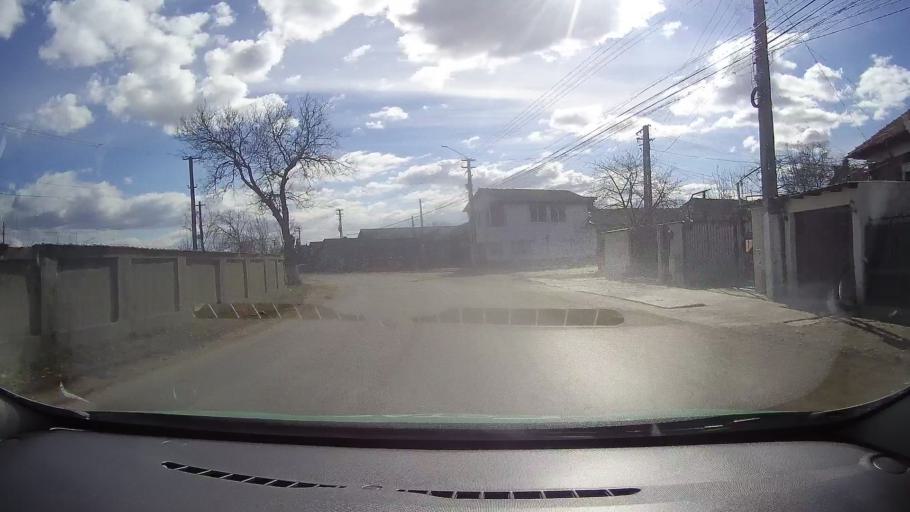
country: RO
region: Dambovita
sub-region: Comuna Doicesti
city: Doicesti
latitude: 44.9865
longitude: 25.3843
